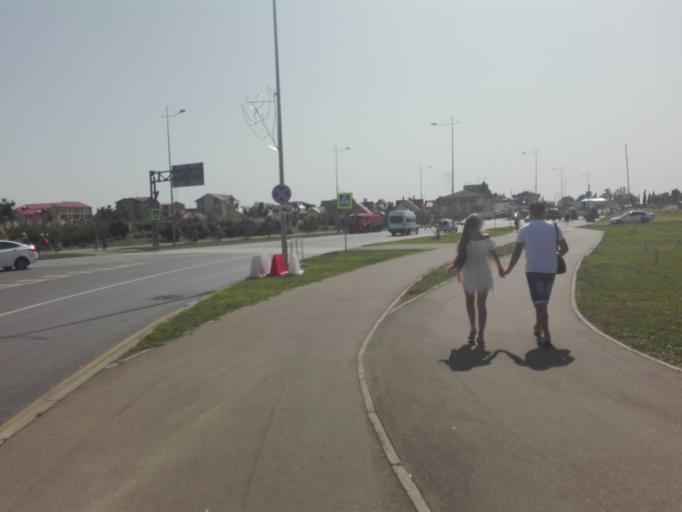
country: RU
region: Krasnodarskiy
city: Adler
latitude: 43.4024
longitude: 39.9689
